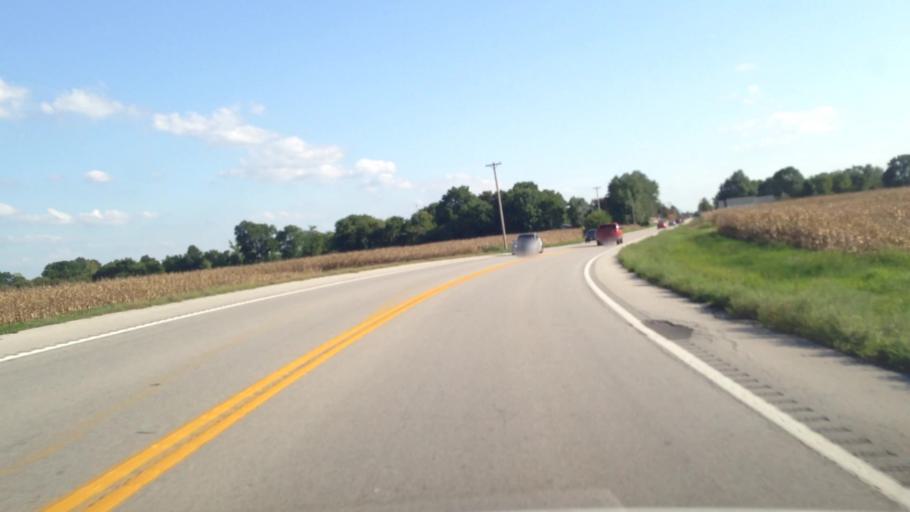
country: US
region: Missouri
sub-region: Jasper County
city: Carl Junction
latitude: 37.2801
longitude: -94.6010
